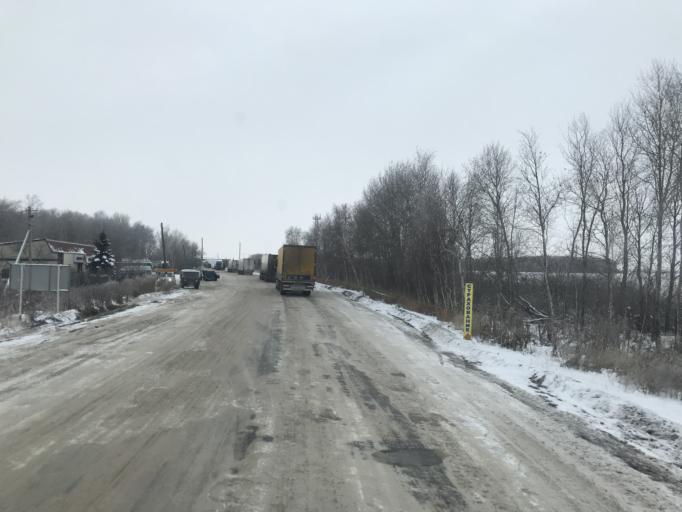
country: RU
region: Kurgan
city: Petukhovo
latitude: 55.0939
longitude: 68.2837
